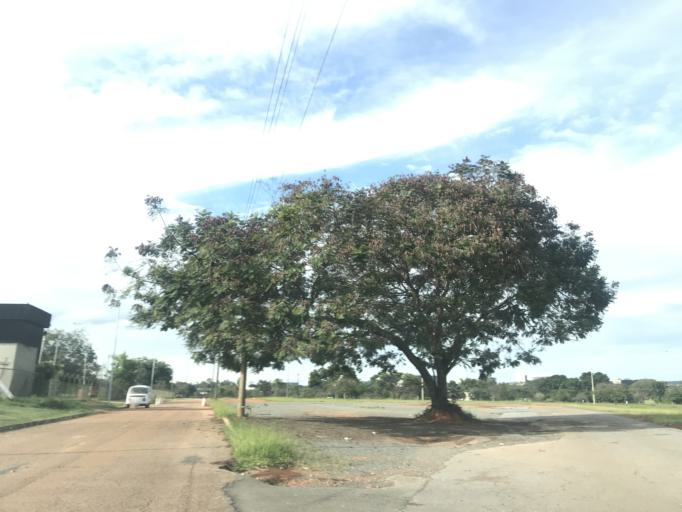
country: BR
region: Federal District
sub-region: Brasilia
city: Brasilia
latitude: -15.8130
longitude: -47.8837
